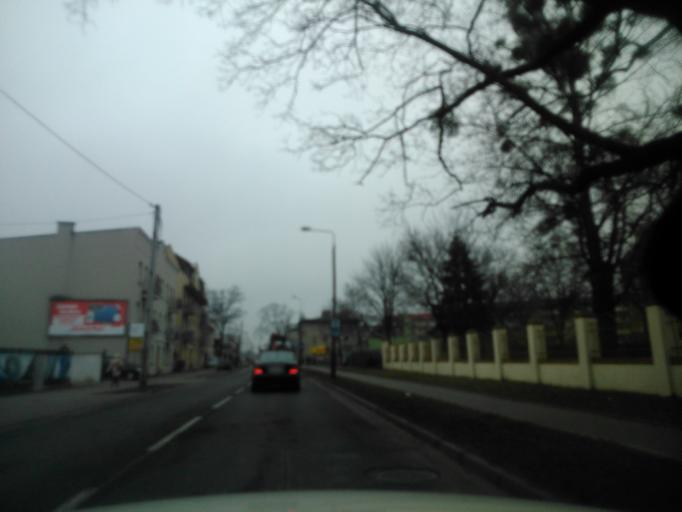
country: PL
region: Kujawsko-Pomorskie
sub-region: Torun
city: Torun
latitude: 53.0221
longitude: 18.6291
